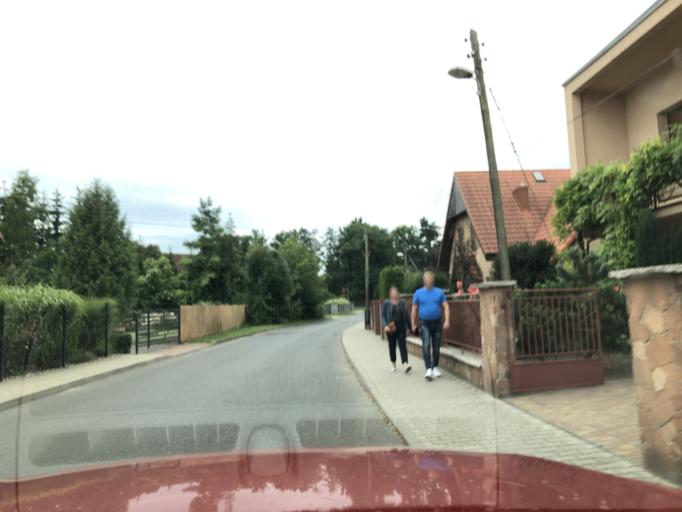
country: PL
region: Greater Poland Voivodeship
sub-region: Powiat szamotulski
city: Pniewy
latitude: 52.5110
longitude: 16.2511
